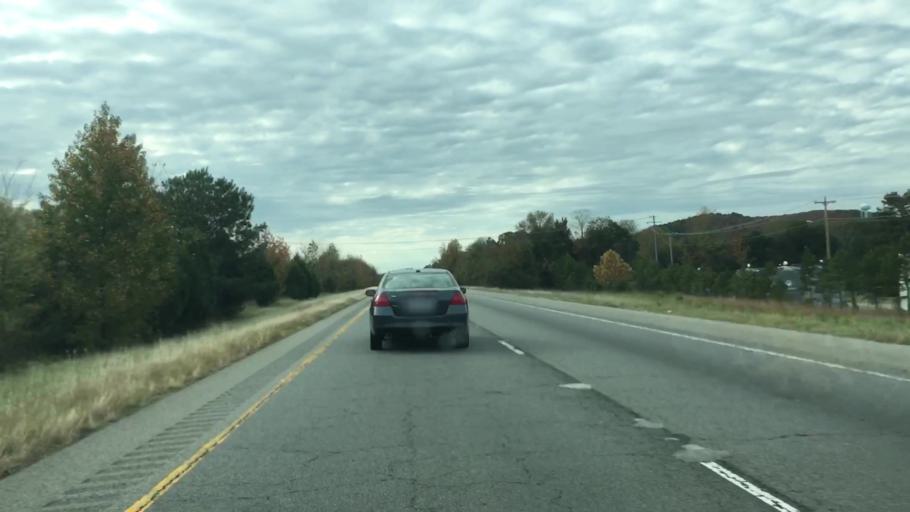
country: US
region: Arkansas
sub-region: Faulkner County
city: Conway
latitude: 35.1198
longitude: -92.4704
